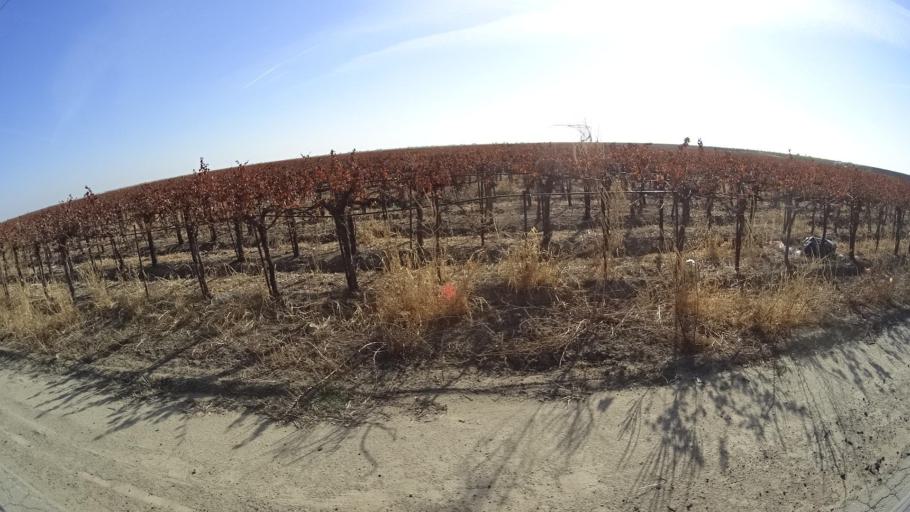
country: US
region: California
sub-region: Kern County
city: Wasco
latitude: 35.7032
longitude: -119.3460
